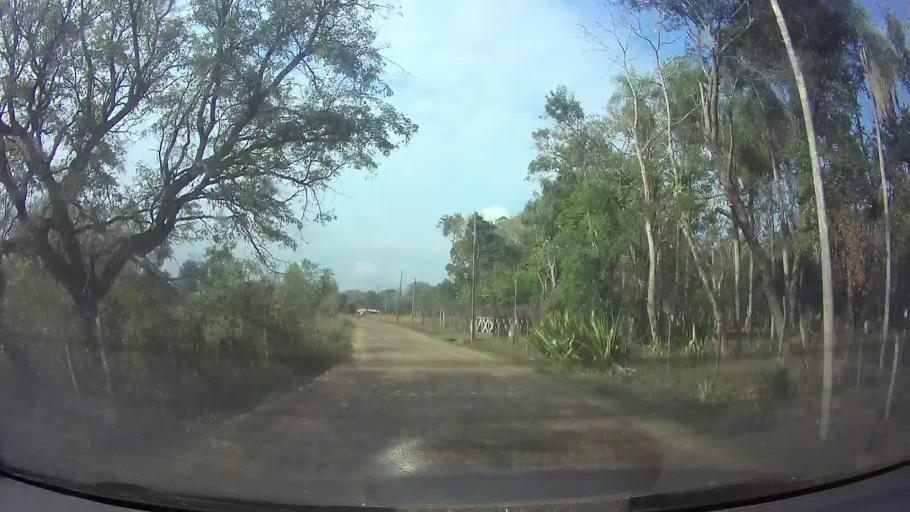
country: PY
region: Cordillera
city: Arroyos y Esteros
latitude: -25.0025
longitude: -57.1972
